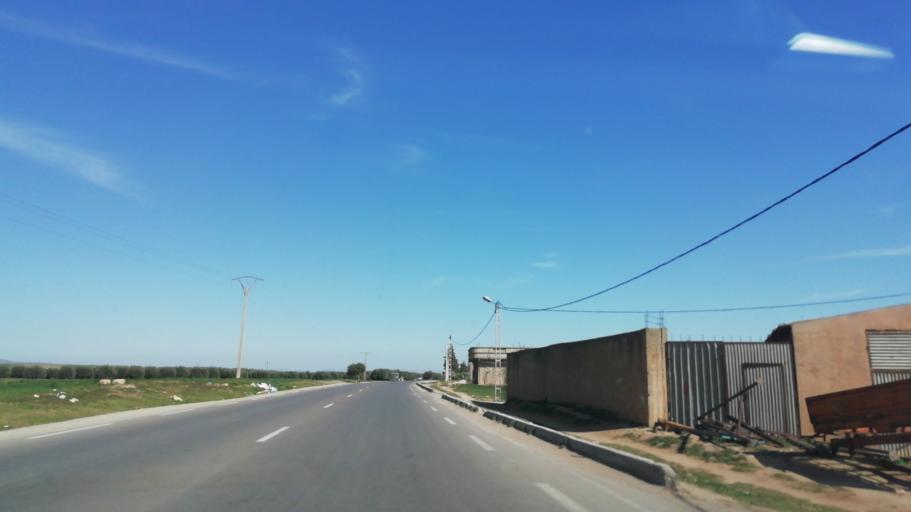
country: DZ
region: Mascara
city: Oued el Abtal
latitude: 35.4249
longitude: 0.4528
